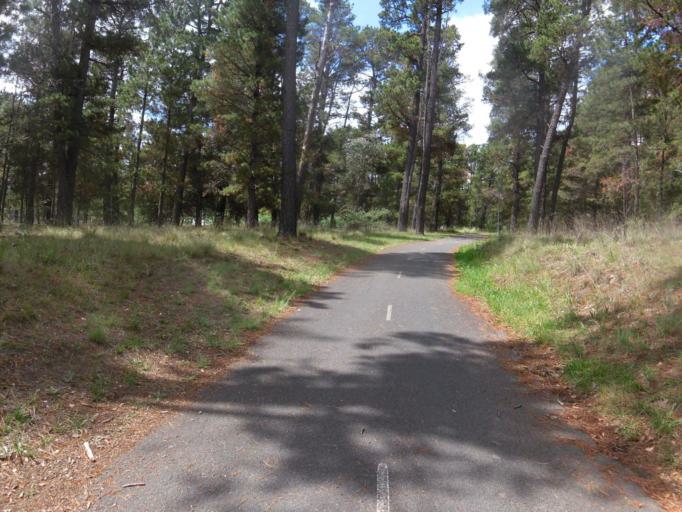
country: AU
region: Australian Capital Territory
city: Macarthur
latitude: -35.4152
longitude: 149.1146
